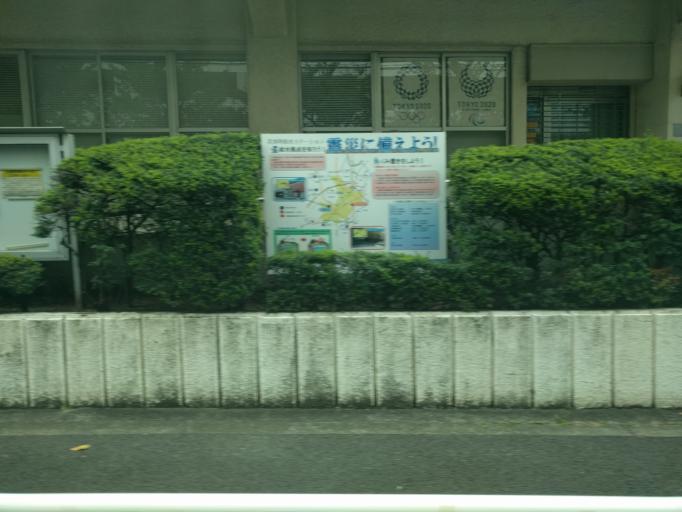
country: JP
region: Tokyo
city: Tokyo
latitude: 35.6330
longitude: 139.6921
